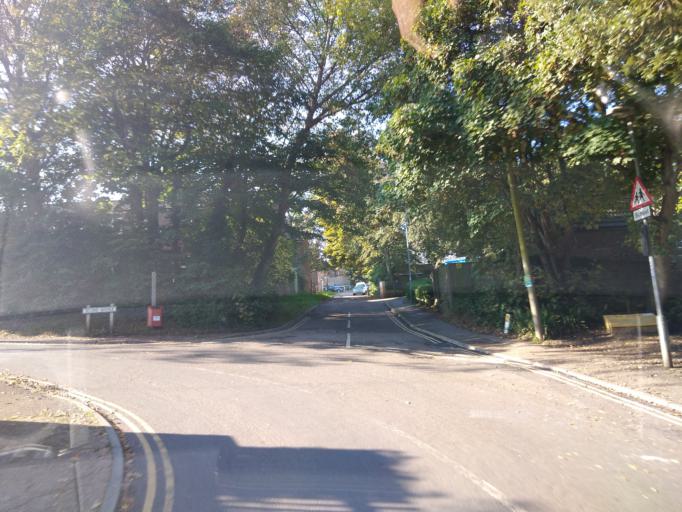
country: GB
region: England
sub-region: East Sussex
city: Newhaven
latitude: 50.7913
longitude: 0.0443
